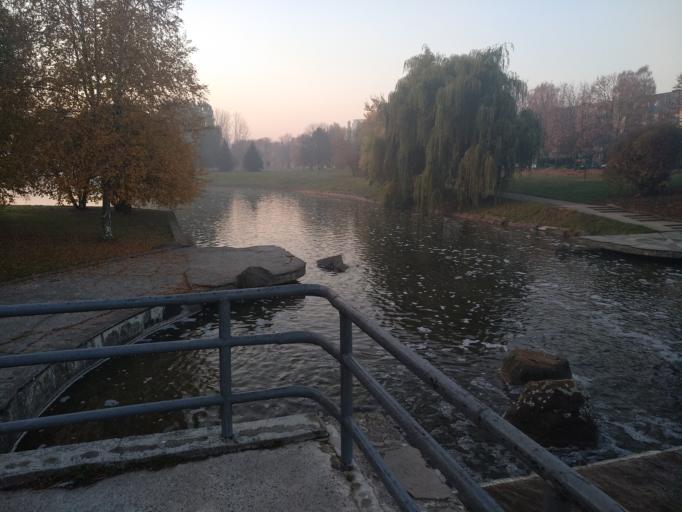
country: BY
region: Minsk
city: Borovlyany
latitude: 53.9469
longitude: 27.6425
